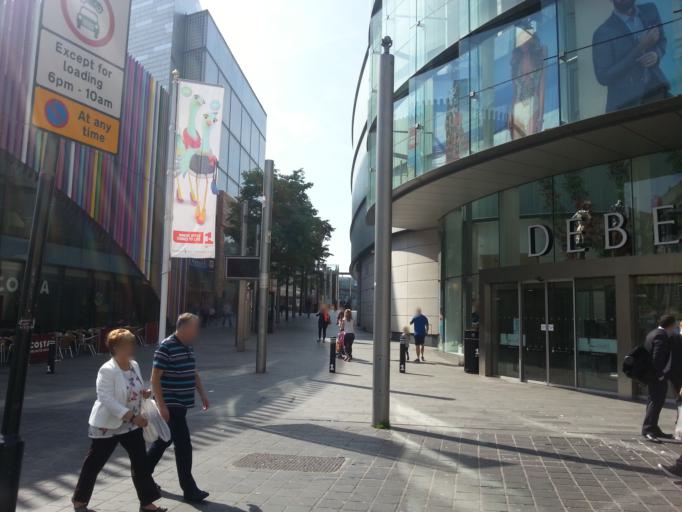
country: GB
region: England
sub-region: Liverpool
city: Liverpool
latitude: 53.4053
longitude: -2.9880
